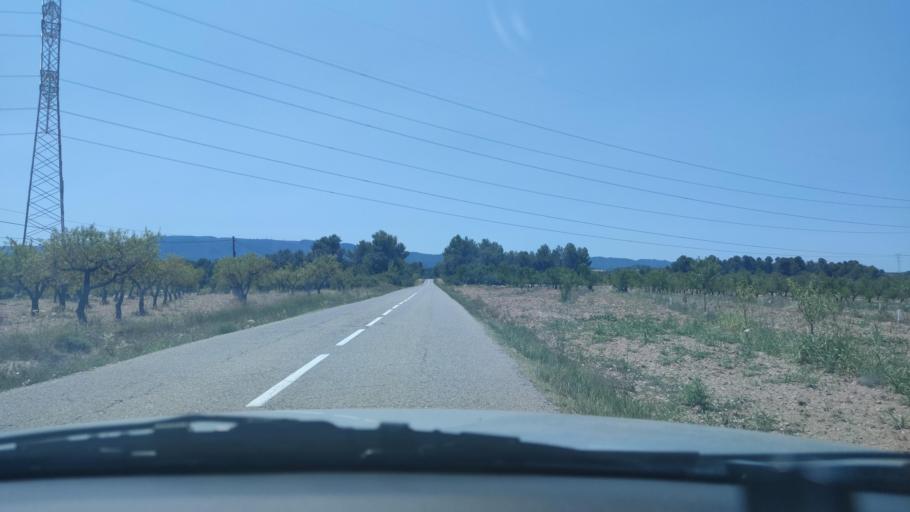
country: ES
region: Catalonia
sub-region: Provincia de Tarragona
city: Vallclara
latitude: 41.4048
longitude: 0.9572
